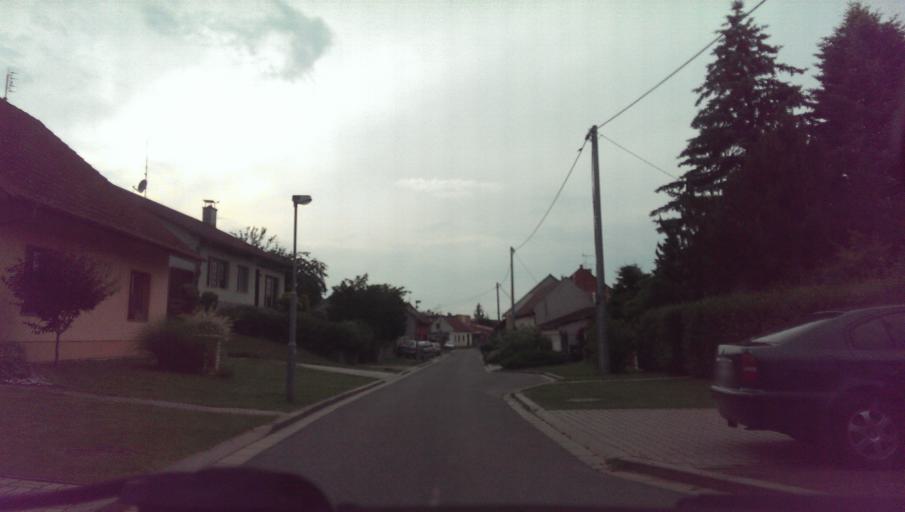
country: CZ
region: Zlin
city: Popovice
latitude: 49.0351
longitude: 17.5056
